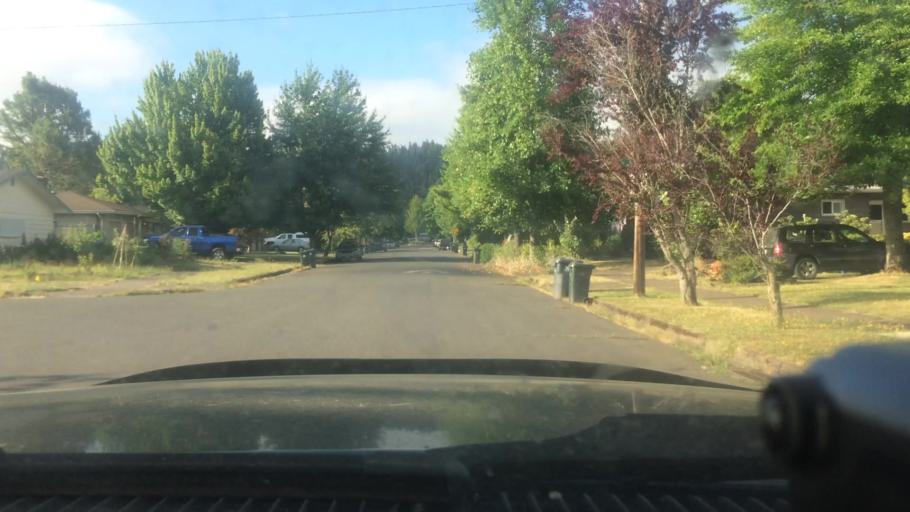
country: US
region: Oregon
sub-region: Lane County
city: Eugene
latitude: 44.0317
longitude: -123.1112
